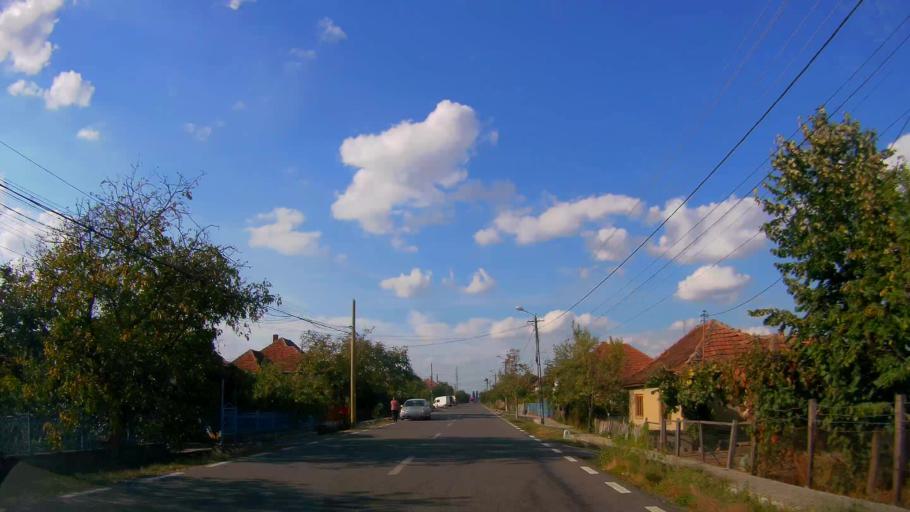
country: RO
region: Satu Mare
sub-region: Comuna Halmeu
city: Halmeu
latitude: 47.9861
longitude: 23.0064
